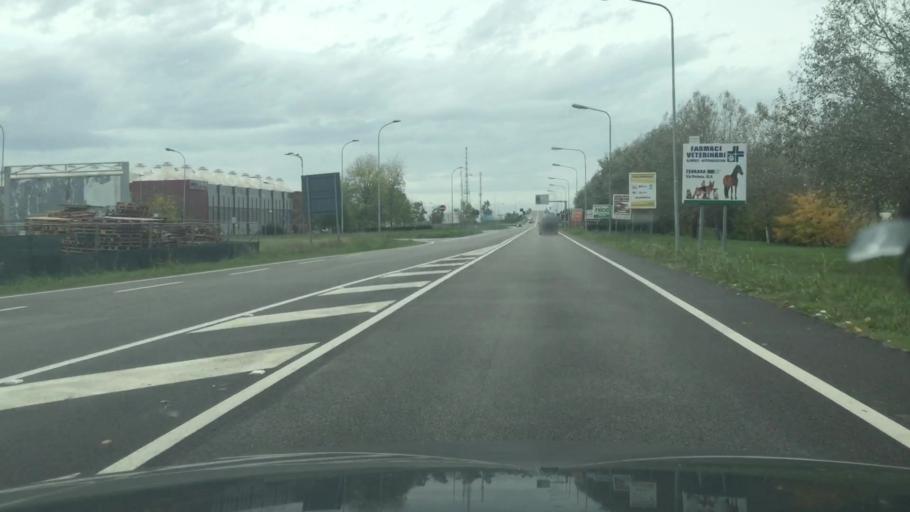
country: IT
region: Emilia-Romagna
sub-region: Provincia di Ferrara
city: Ferrara
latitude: 44.8217
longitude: 11.5964
